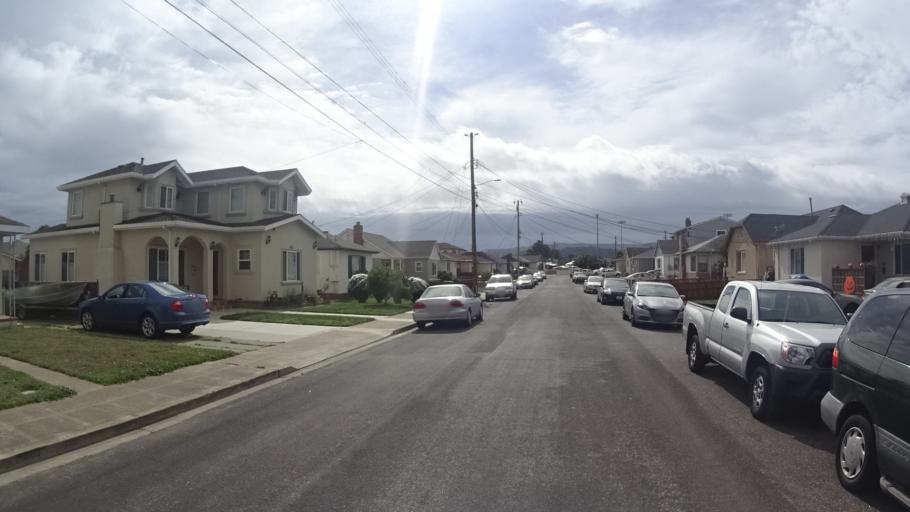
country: US
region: California
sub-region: San Mateo County
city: South San Francisco
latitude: 37.6505
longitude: -122.4227
